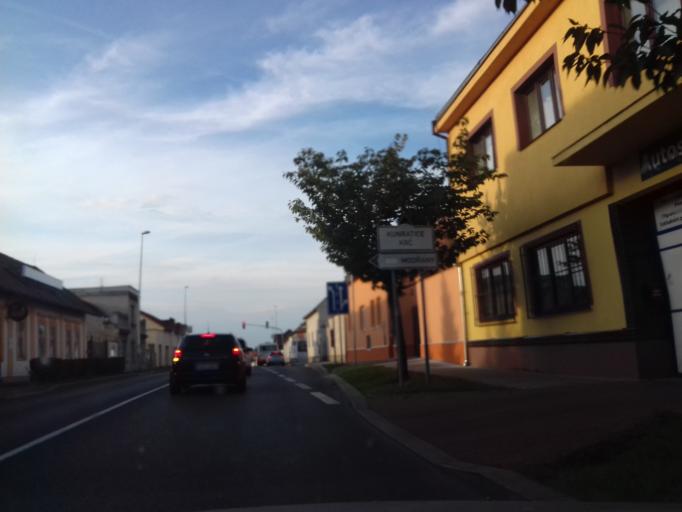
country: CZ
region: Central Bohemia
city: Dolni Brezany
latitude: 50.0053
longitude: 14.4641
